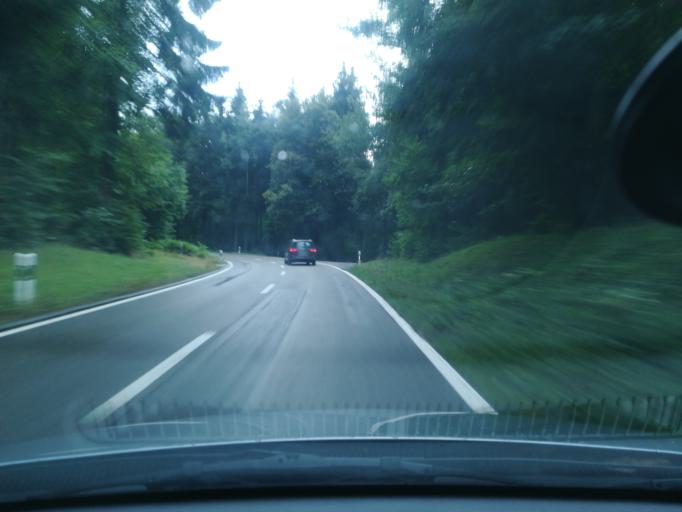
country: CH
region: Thurgau
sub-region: Frauenfeld District
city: Huttwilen
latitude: 47.6178
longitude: 8.8834
